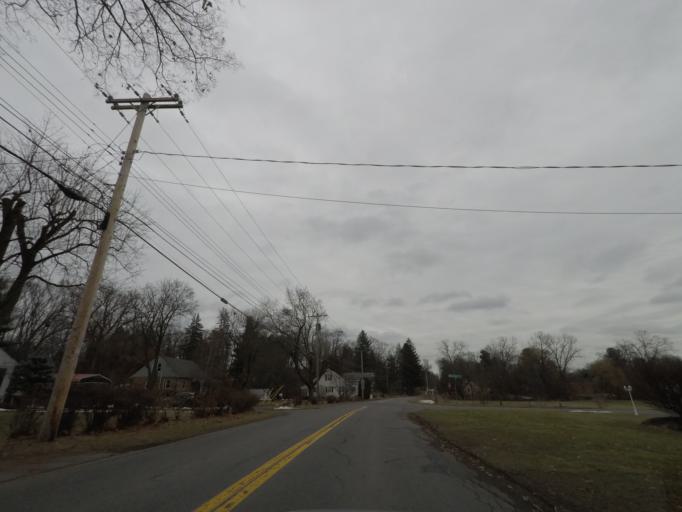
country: US
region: New York
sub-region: Schenectady County
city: Schenectady
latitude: 42.7857
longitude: -73.9005
